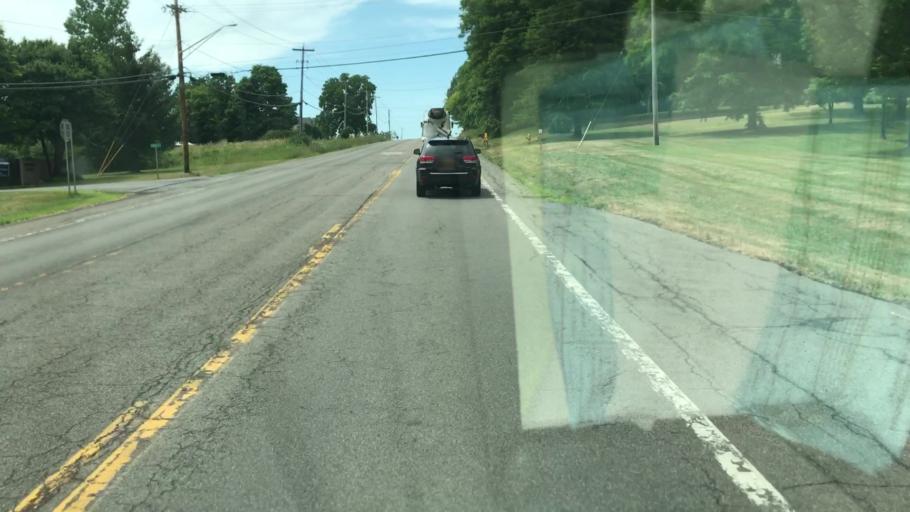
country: US
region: New York
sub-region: Onondaga County
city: Skaneateles
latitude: 42.9453
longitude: -76.3974
